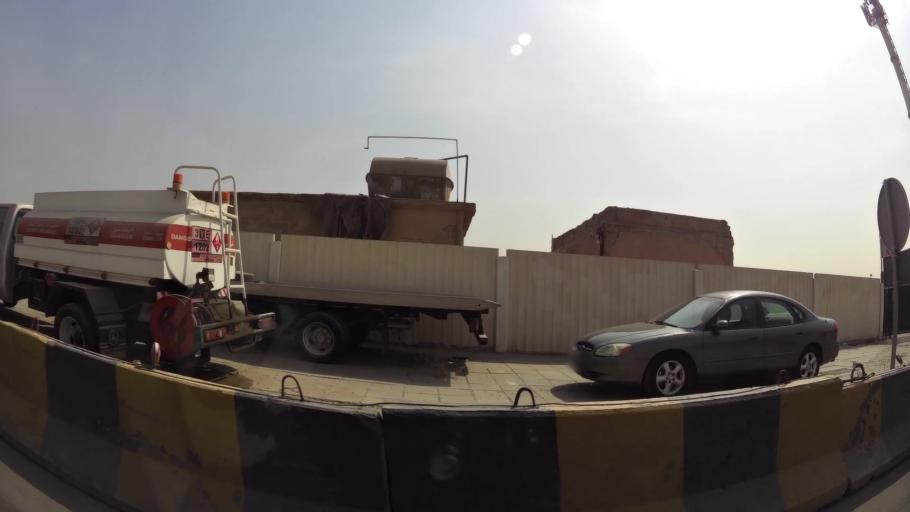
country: KW
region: Al Asimah
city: Ash Shamiyah
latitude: 29.3363
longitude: 47.9416
